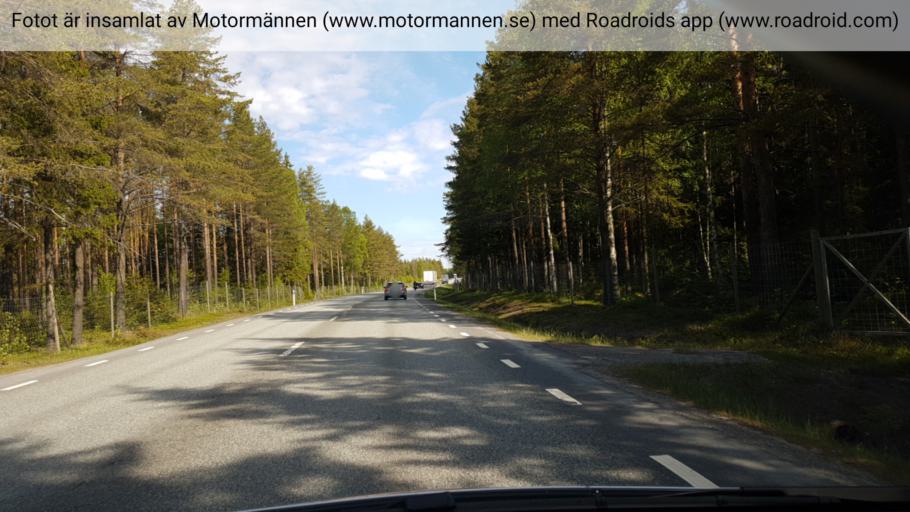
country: SE
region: Vaesterbotten
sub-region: Skelleftea Kommun
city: Burea
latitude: 64.5275
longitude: 21.2582
